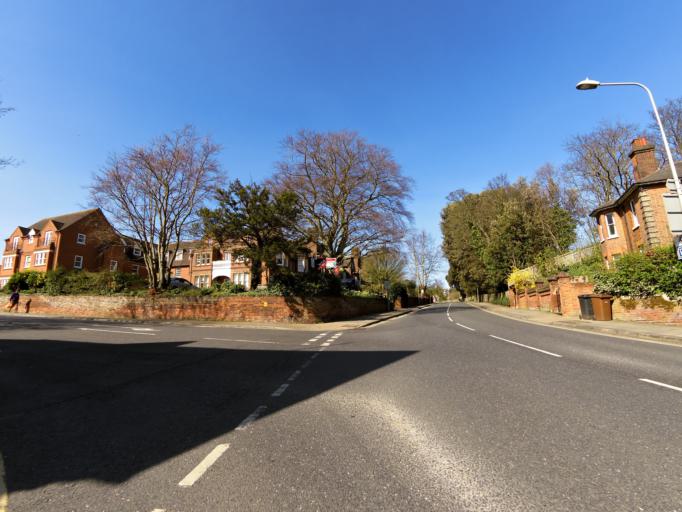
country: GB
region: England
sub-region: Suffolk
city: Ipswich
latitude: 52.0624
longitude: 1.1514
